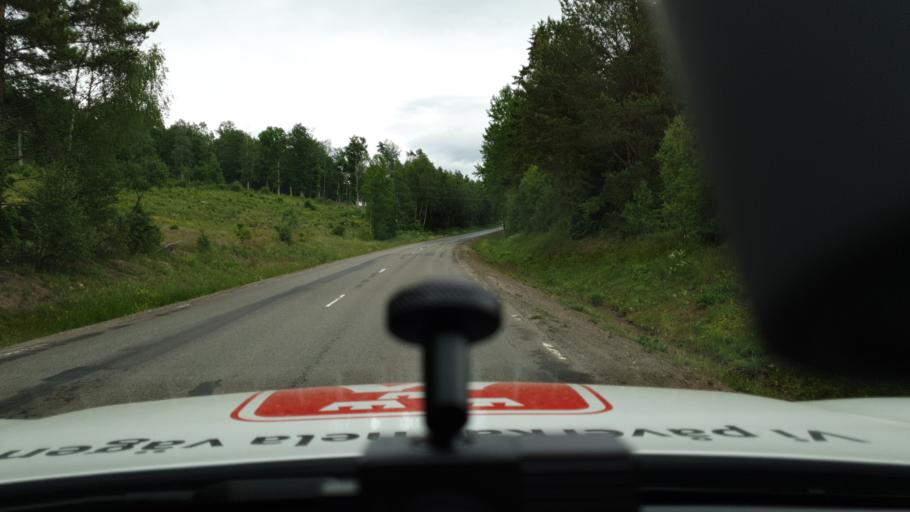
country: SE
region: Joenkoeping
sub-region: Mullsjo Kommun
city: Mullsjoe
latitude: 57.9867
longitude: 13.7937
